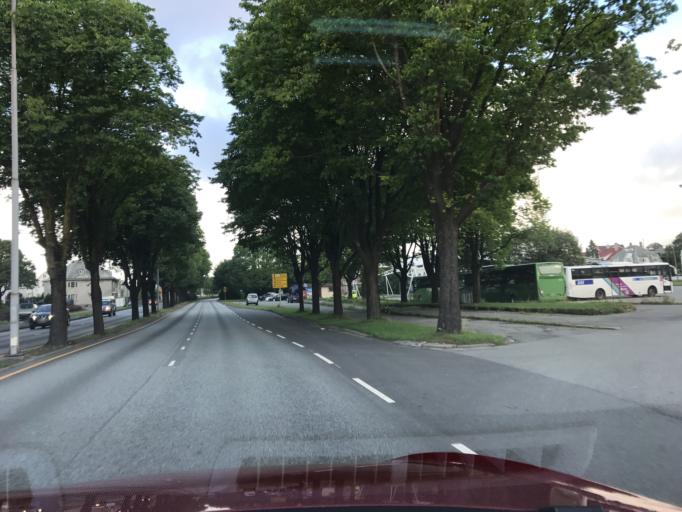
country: NO
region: Rogaland
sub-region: Haugesund
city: Haugesund
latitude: 59.4150
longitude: 5.2751
